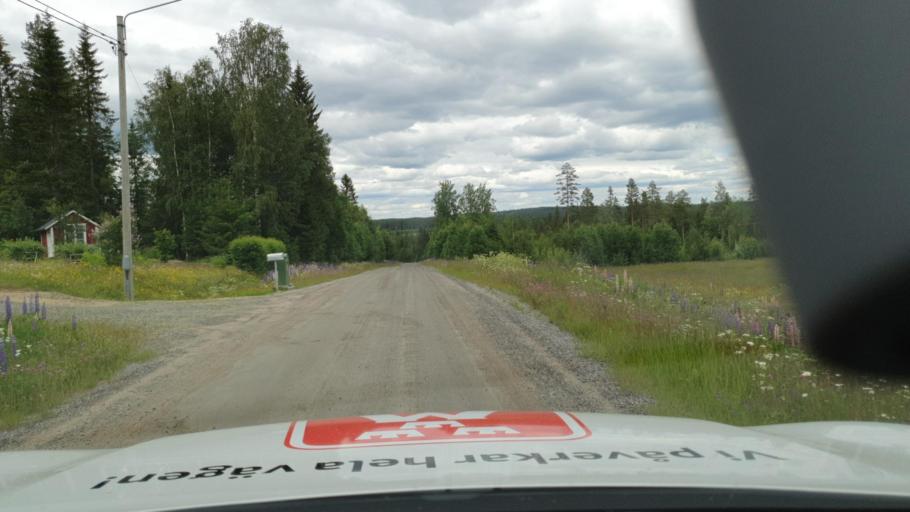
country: SE
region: Vaesterbotten
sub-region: Bjurholms Kommun
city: Bjurholm
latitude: 63.7499
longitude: 19.2735
